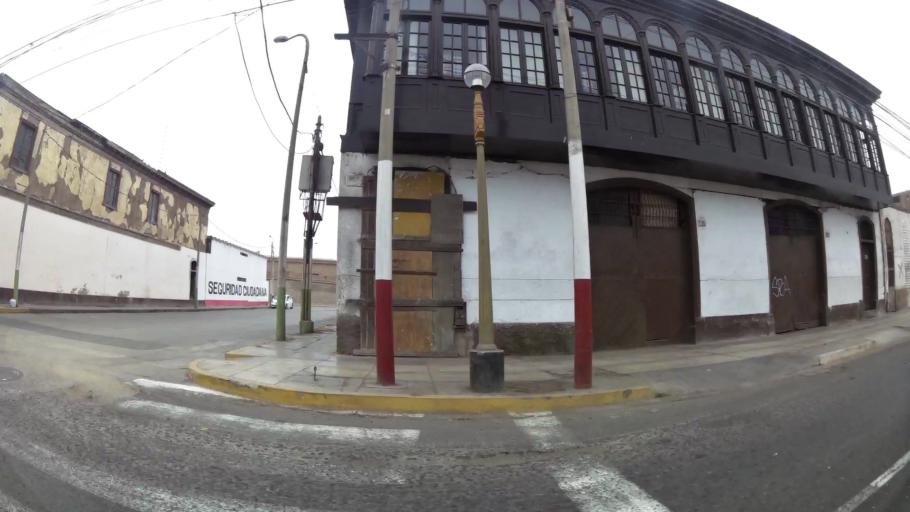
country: PE
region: Callao
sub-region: Callao
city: Callao
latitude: -12.0648
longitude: -77.1478
